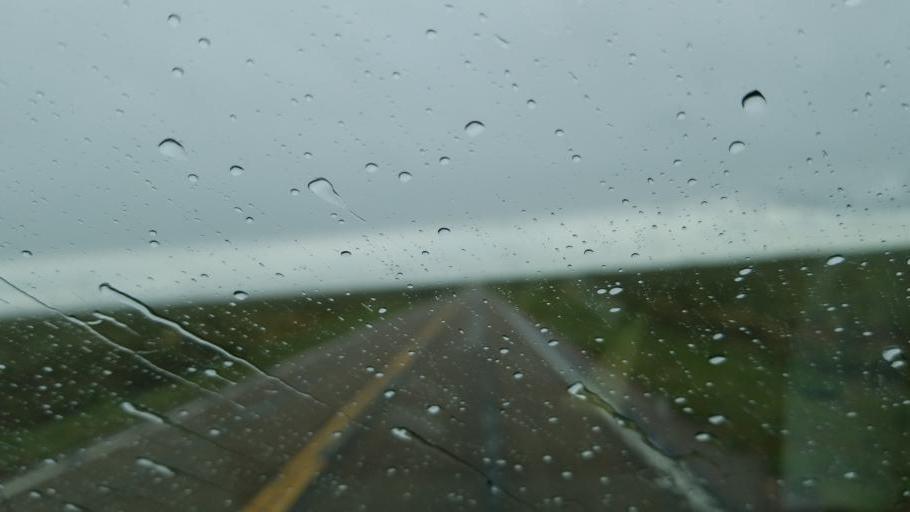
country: US
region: Colorado
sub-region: Lincoln County
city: Hugo
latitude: 38.8495
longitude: -103.2171
